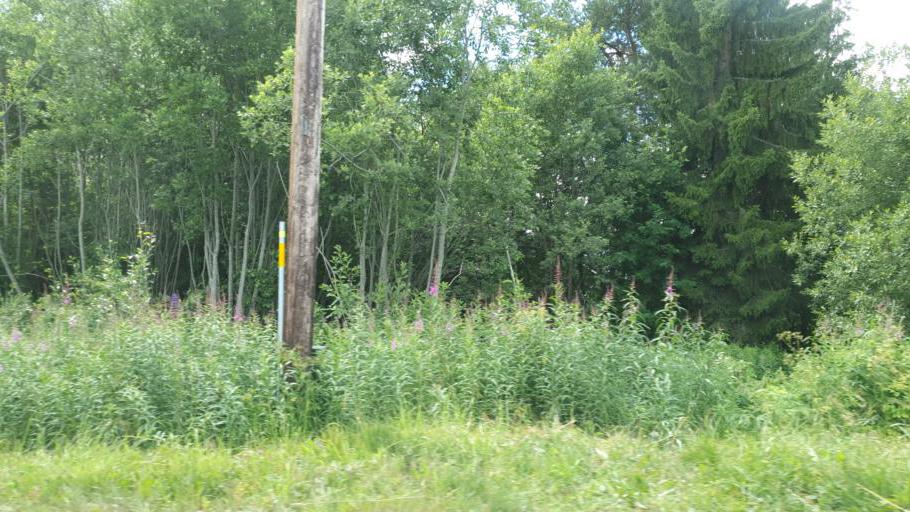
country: NO
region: Sor-Trondelag
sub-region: Rennebu
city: Berkak
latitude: 62.8330
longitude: 10.0066
